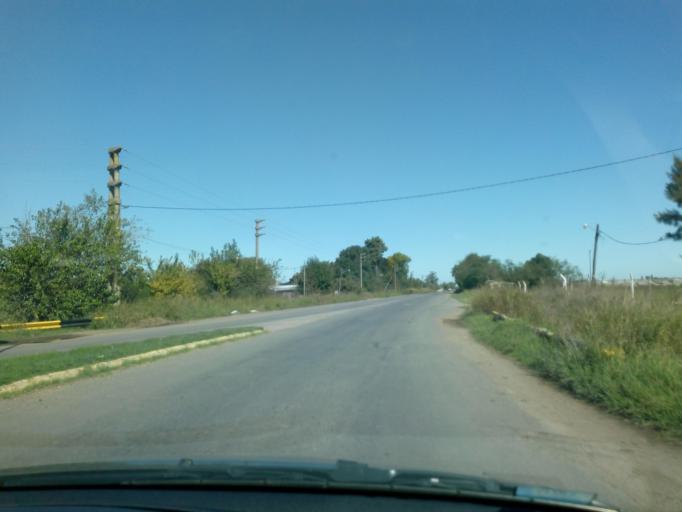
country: AR
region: Buenos Aires
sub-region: Partido de La Plata
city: La Plata
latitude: -35.0056
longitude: -58.0224
